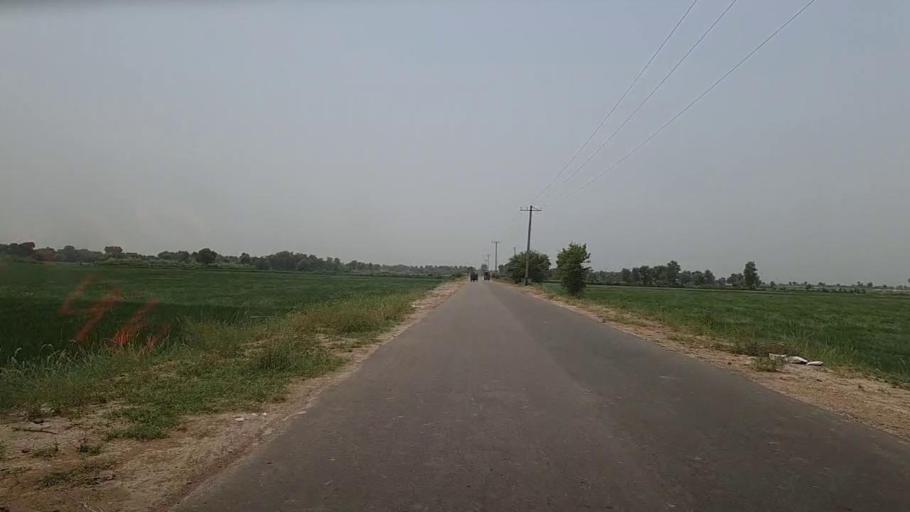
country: PK
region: Sindh
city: Sita Road
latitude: 27.0495
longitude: 67.9016
